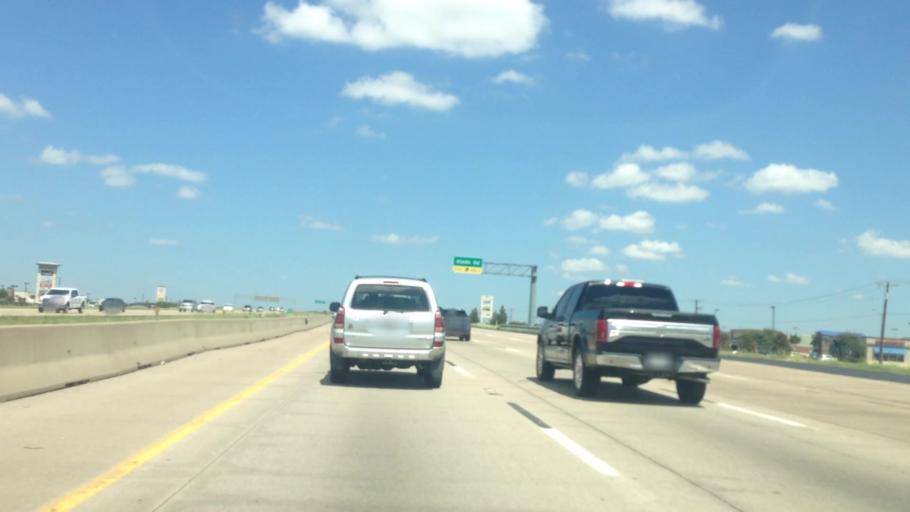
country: US
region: Texas
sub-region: Tarrant County
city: Euless
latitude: 32.8744
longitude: -97.0995
